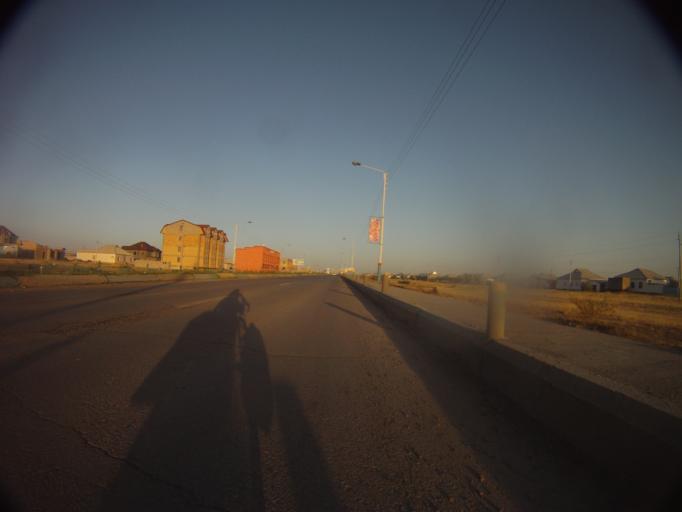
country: KZ
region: Ongtustik Qazaqstan
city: Turkestan
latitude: 43.2810
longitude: 68.3190
